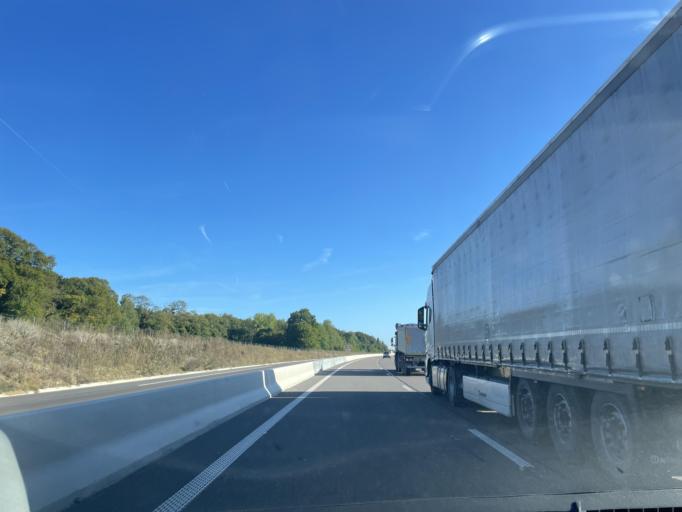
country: FR
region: Picardie
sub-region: Departement de l'Oise
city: Peroy-les-Gombries
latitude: 49.1657
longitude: 2.8620
